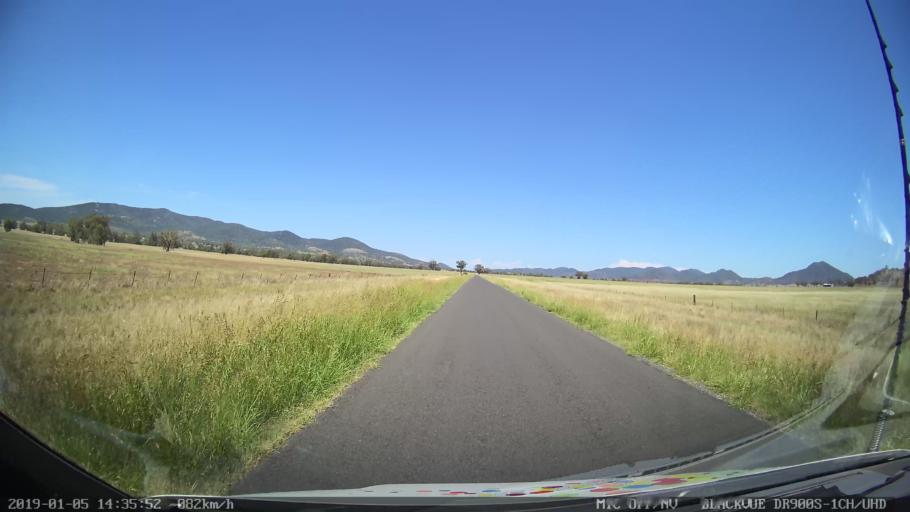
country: AU
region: New South Wales
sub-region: Tamworth Municipality
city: Phillip
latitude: -31.2427
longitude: 150.6559
